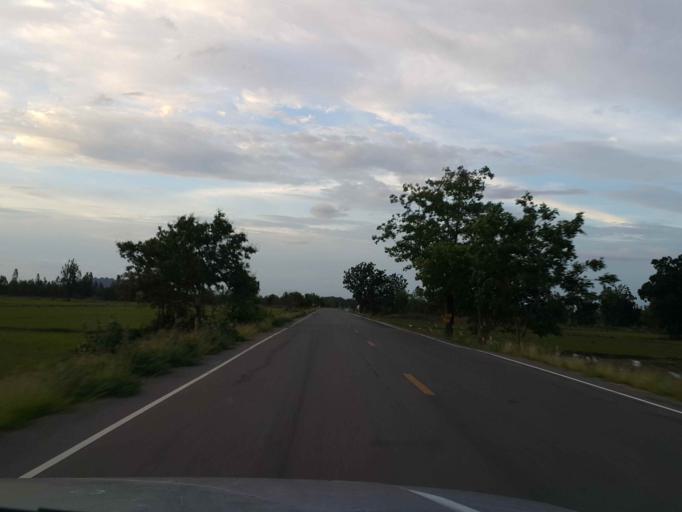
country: TH
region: Sukhothai
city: Ban Dan Lan Hoi
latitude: 17.0903
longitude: 99.5894
